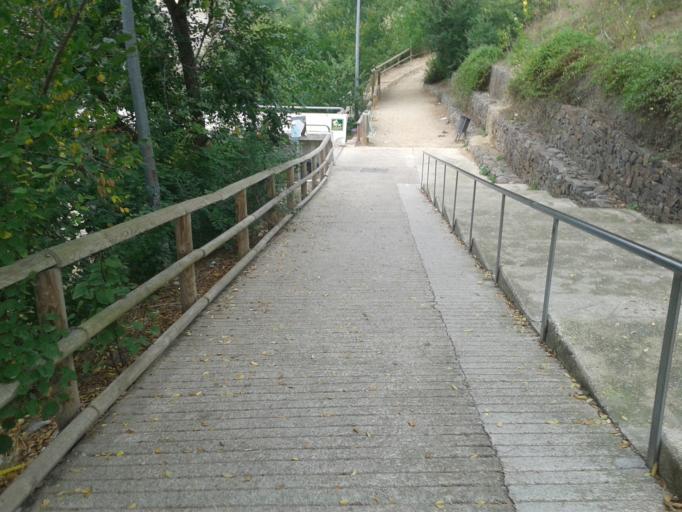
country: ES
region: Catalonia
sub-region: Provincia de Barcelona
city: Sentmenat
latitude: 41.6101
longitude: 2.1343
